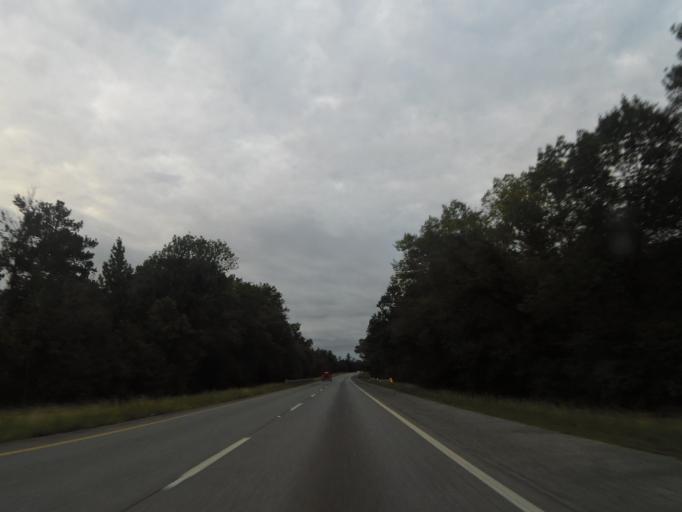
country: US
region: Alabama
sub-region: Saint Clair County
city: Steele
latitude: 33.9115
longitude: -86.2199
